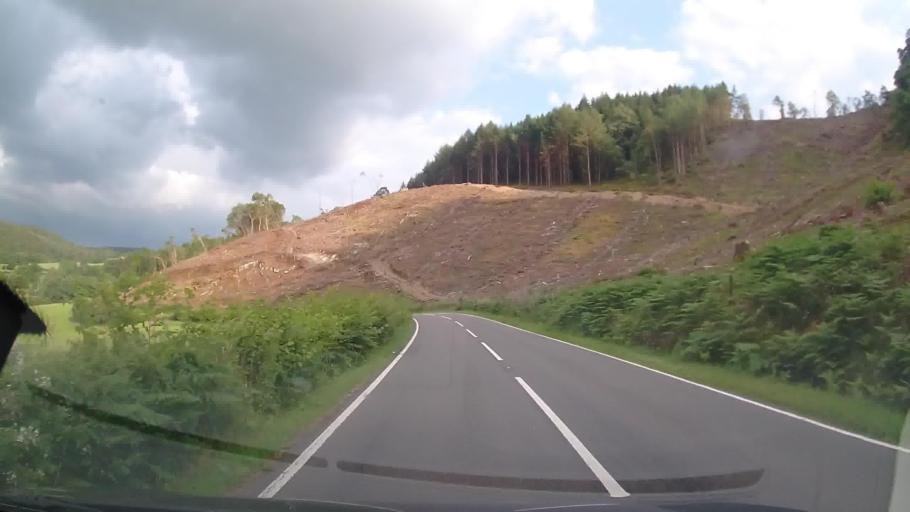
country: GB
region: Wales
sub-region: Gwynedd
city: Bala
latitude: 52.9073
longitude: -3.5339
